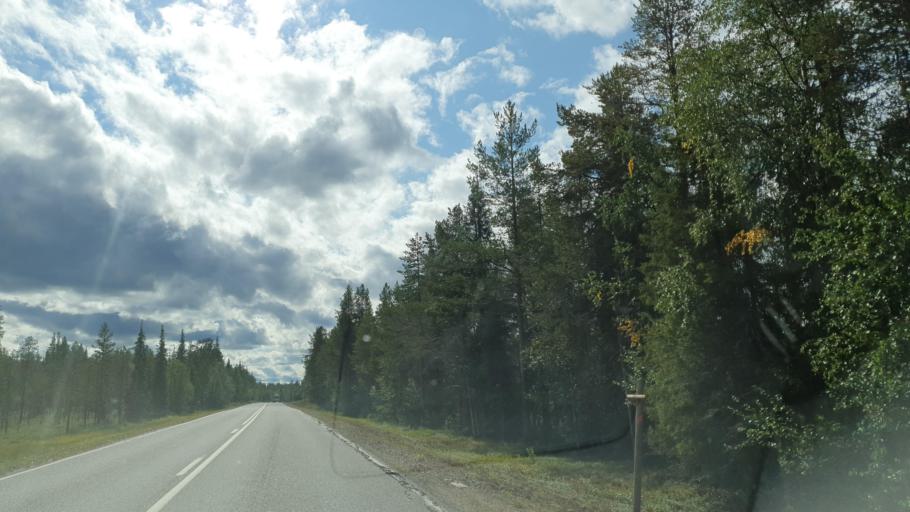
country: FI
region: Lapland
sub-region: Tunturi-Lappi
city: Muonio
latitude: 67.8801
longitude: 24.2080
